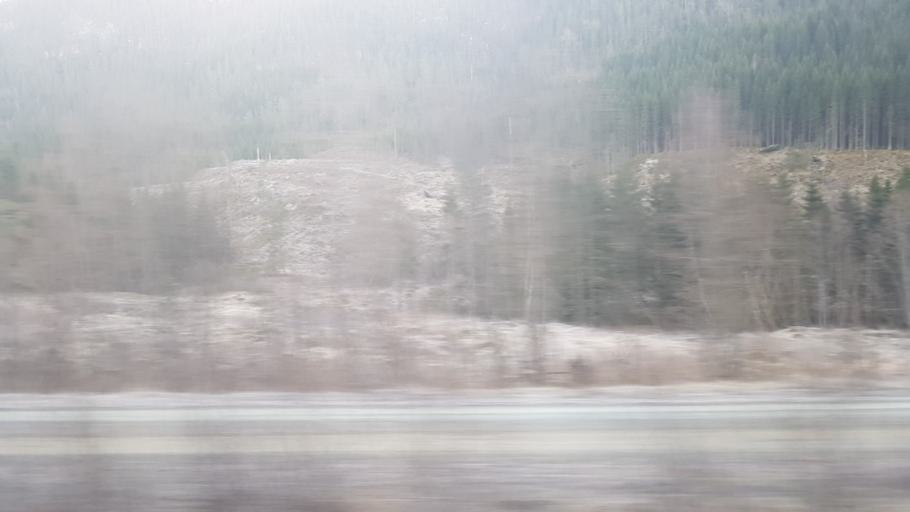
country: NO
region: Nord-Trondelag
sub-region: Stjordal
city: Stjordalshalsen
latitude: 63.5906
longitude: 11.0132
